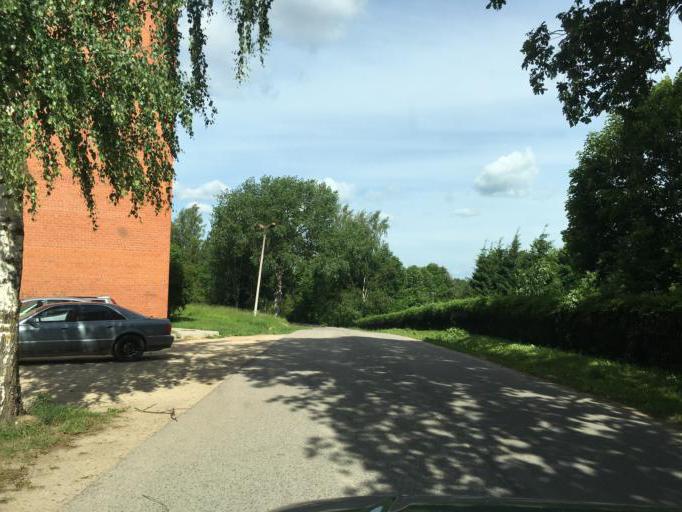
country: LV
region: Balvu Rajons
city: Balvi
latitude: 57.1339
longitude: 27.2711
